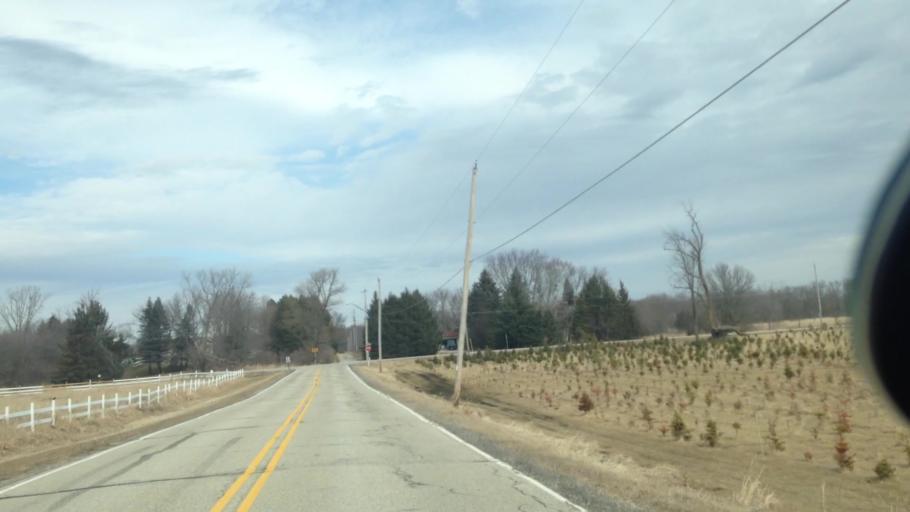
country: US
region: Wisconsin
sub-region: Waukesha County
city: Sussex
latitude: 43.1615
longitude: -88.2233
